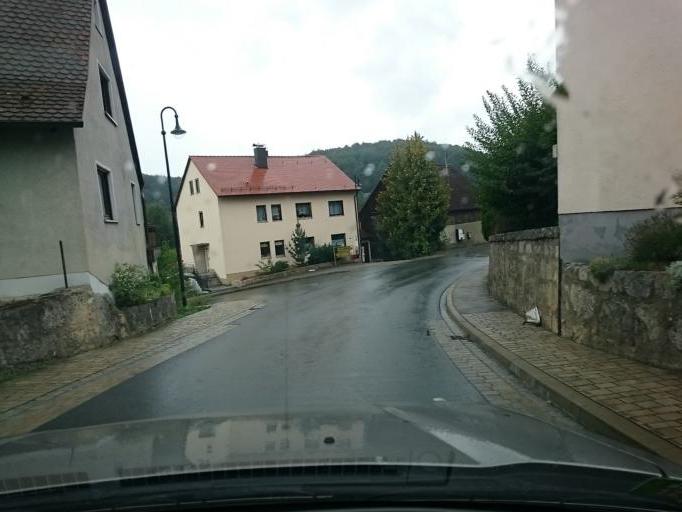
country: DE
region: Bavaria
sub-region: Upper Franconia
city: Obertrubach
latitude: 49.6814
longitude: 11.4176
